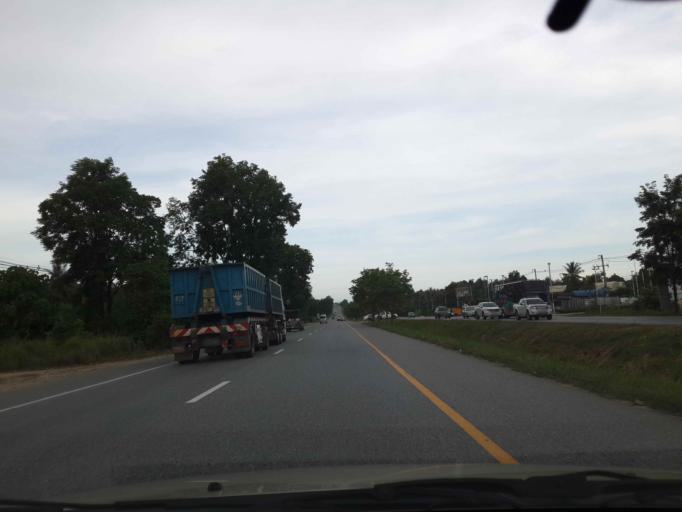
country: TH
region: Chon Buri
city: Phatthaya
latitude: 12.9402
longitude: 100.9956
